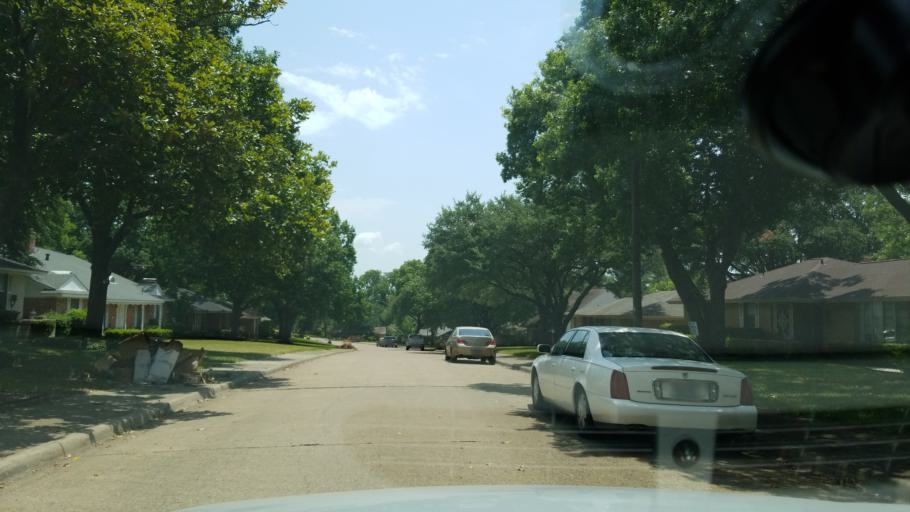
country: US
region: Texas
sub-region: Dallas County
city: Cockrell Hill
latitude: 32.6792
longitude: -96.8383
